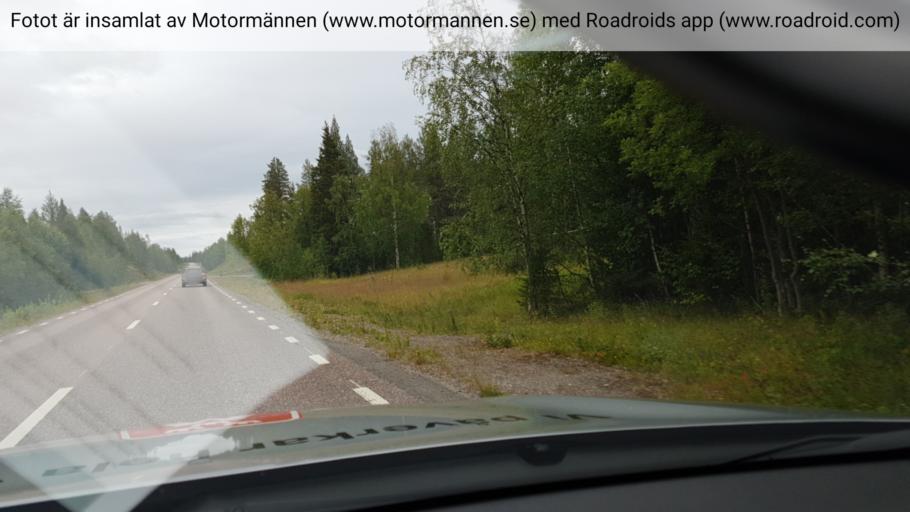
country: SE
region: Norrbotten
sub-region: Gallivare Kommun
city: Gaellivare
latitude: 67.0532
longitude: 21.5959
